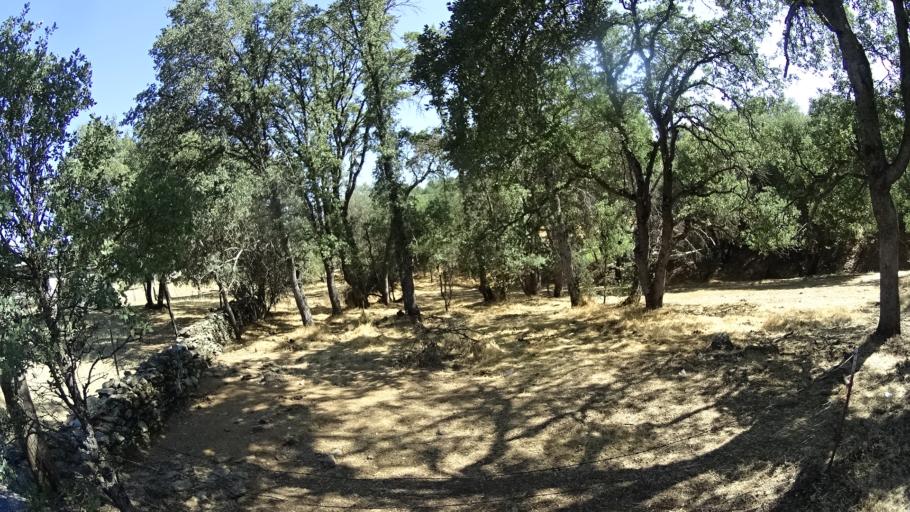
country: US
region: California
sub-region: Calaveras County
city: Angels Camp
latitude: 38.0773
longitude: -120.5450
